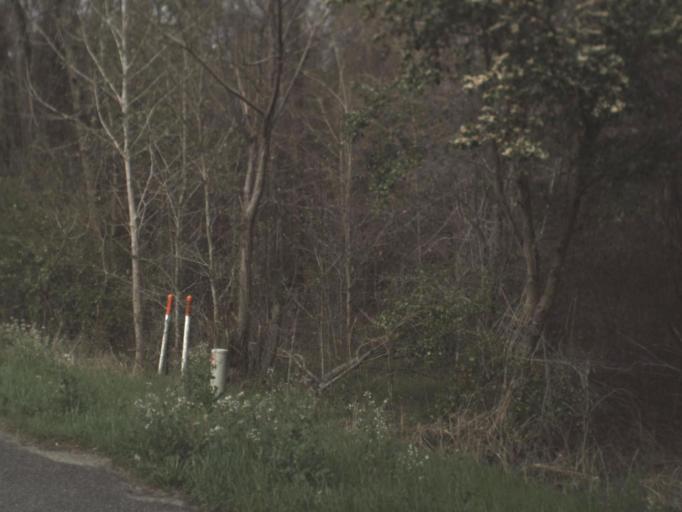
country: US
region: Florida
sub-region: Leon County
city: Tallahassee
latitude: 30.4955
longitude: -84.1071
